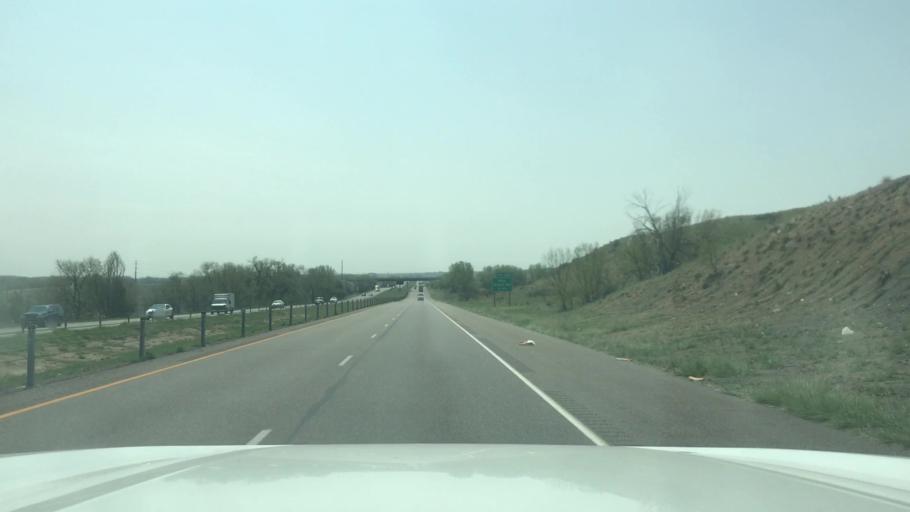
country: US
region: Colorado
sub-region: El Paso County
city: Fountain
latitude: 38.6424
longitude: -104.6938
